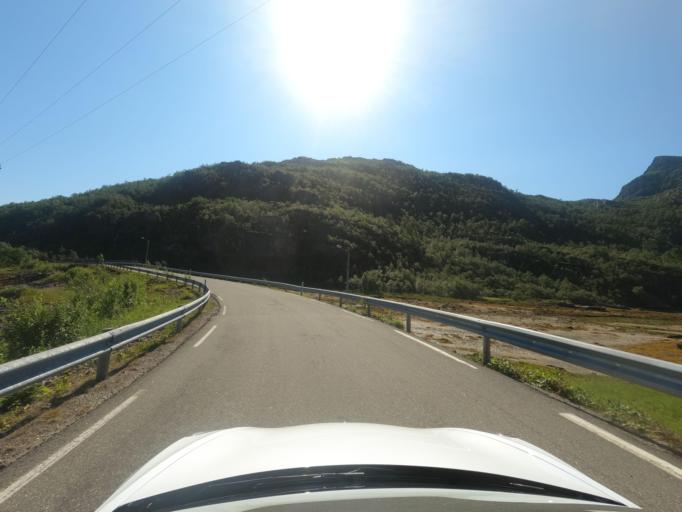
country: NO
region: Nordland
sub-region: Hadsel
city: Stokmarknes
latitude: 68.2996
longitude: 15.0380
